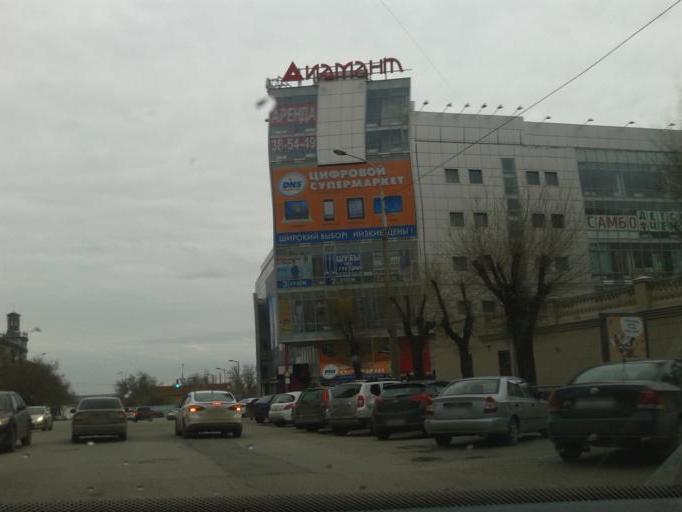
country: RU
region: Volgograd
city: Volgograd
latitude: 48.7086
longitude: 44.5214
